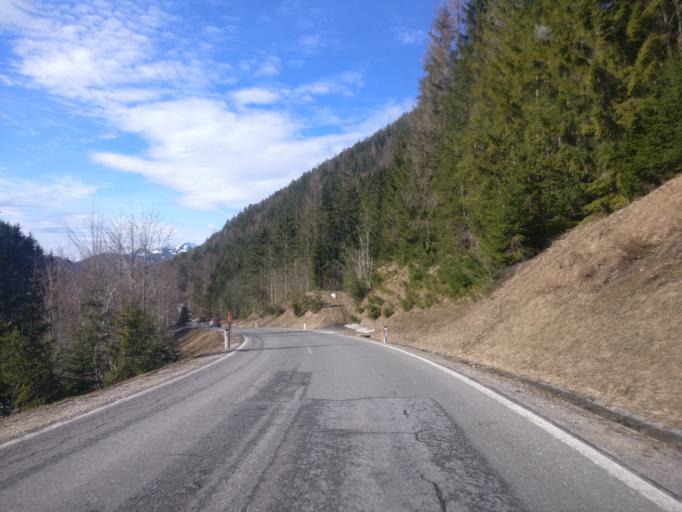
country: AT
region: Styria
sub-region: Politischer Bezirk Liezen
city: Landl
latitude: 47.6581
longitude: 14.6598
